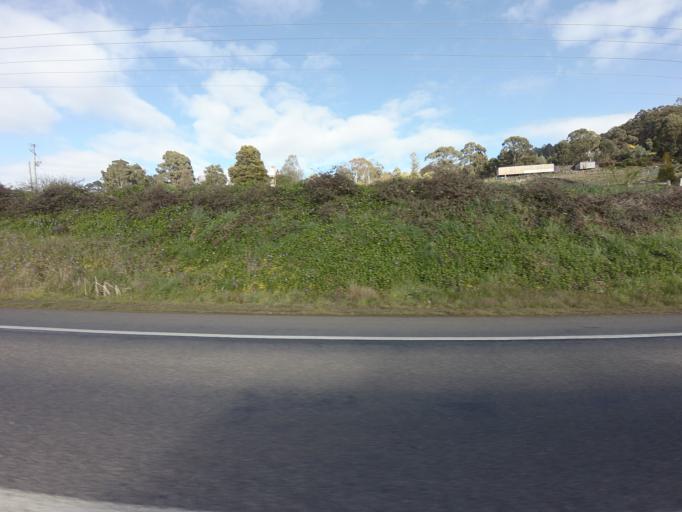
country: AU
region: Tasmania
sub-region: Huon Valley
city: Franklin
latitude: -43.1065
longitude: 147.0005
